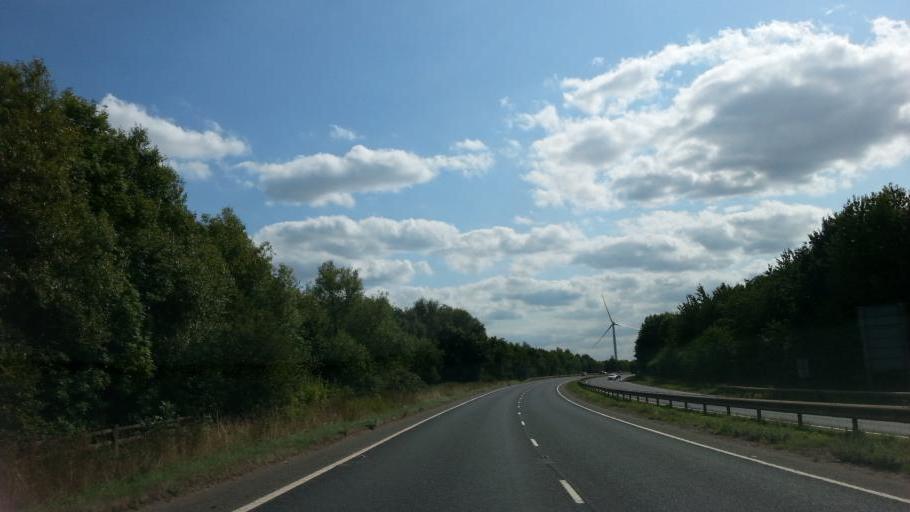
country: GB
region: England
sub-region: Leicestershire
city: Mountsorrel
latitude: 52.7132
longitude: -1.1247
